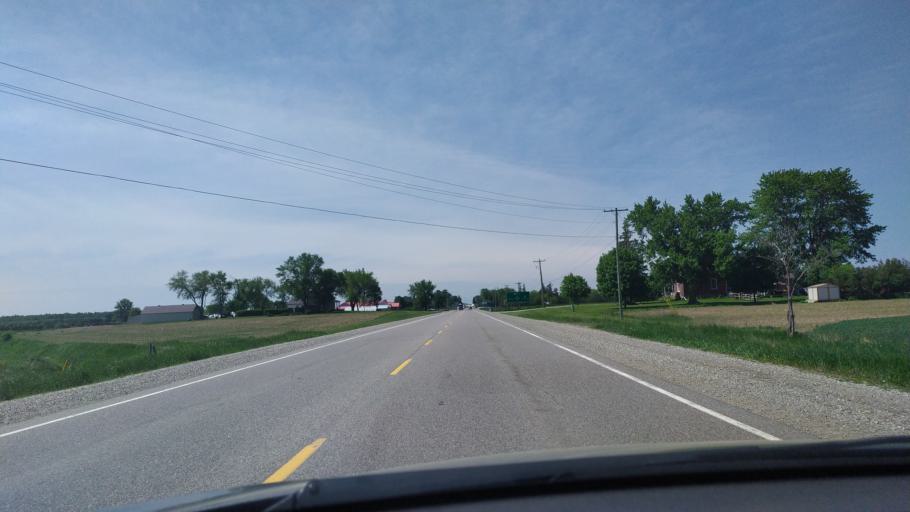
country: CA
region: Ontario
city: Stratford
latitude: 43.3129
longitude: -81.0320
